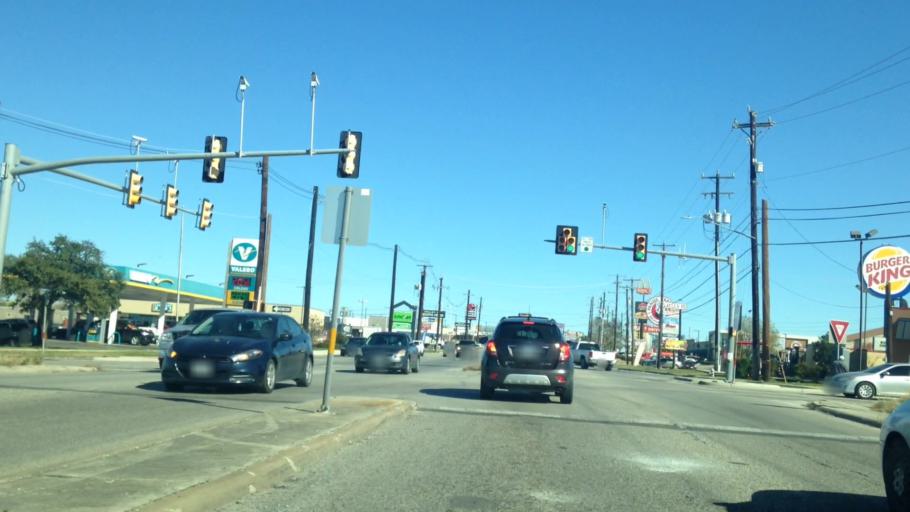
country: US
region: Texas
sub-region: Bexar County
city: Lackland Air Force Base
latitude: 29.3805
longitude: -98.6414
